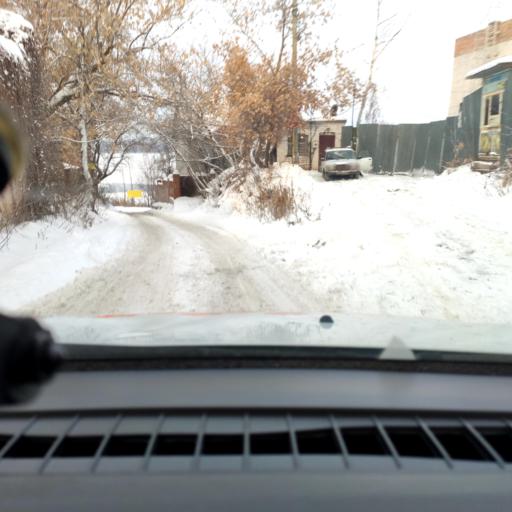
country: RU
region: Samara
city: Samara
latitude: 53.2801
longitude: 50.1895
